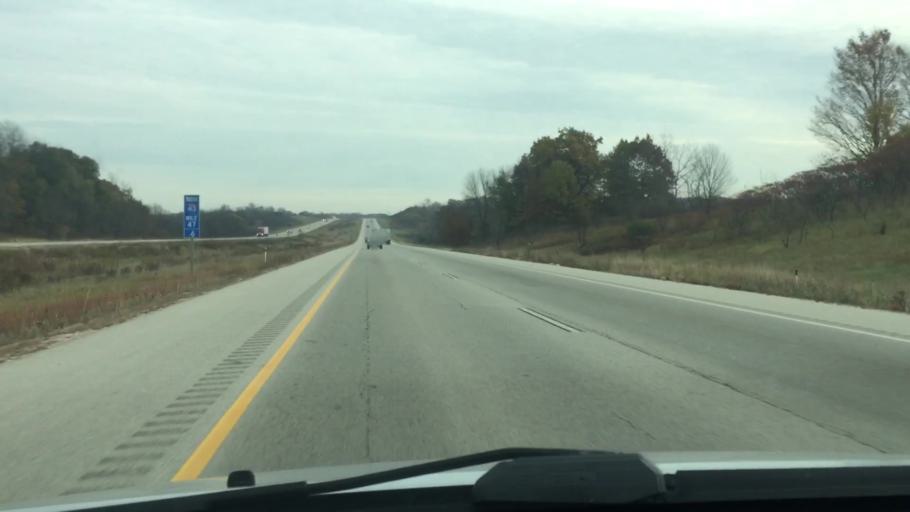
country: US
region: Wisconsin
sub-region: Waukesha County
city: Big Bend
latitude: 42.8887
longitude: -88.2690
